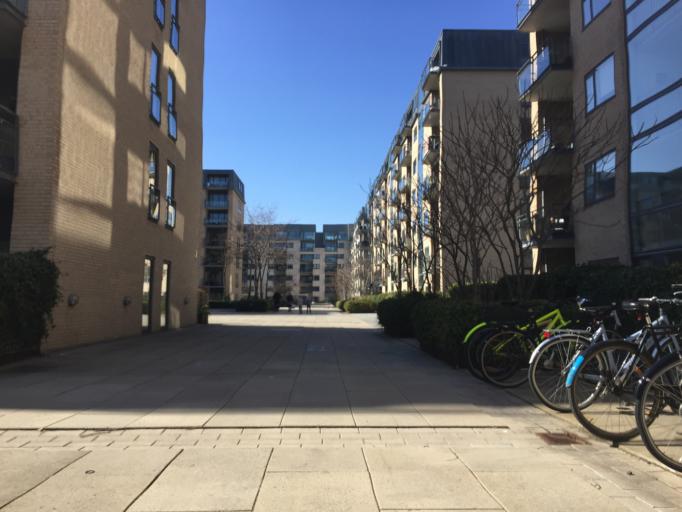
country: DK
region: Capital Region
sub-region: Kobenhavn
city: Christianshavn
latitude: 55.6662
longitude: 12.5841
